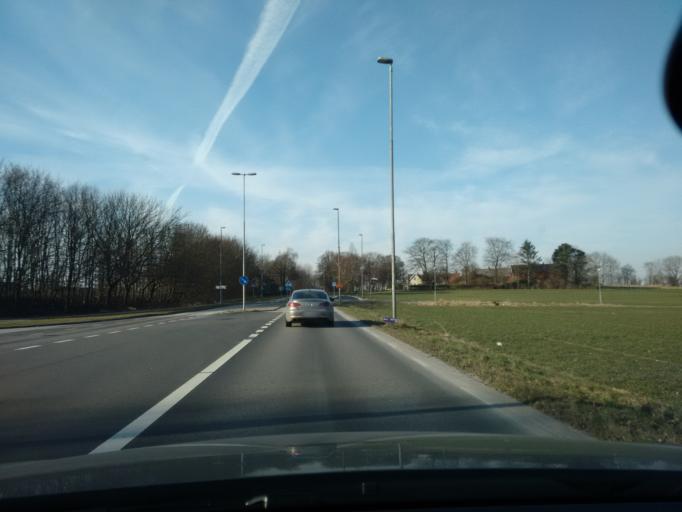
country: SE
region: Skane
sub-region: Lunds Kommun
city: Lund
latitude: 55.7288
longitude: 13.1786
